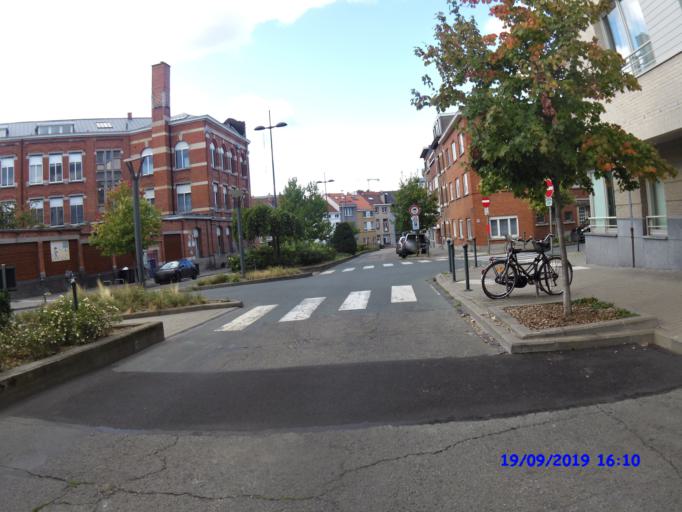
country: BE
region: Brussels Capital
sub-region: Bruxelles-Capitale
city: Brussels
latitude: 50.8350
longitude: 4.3968
